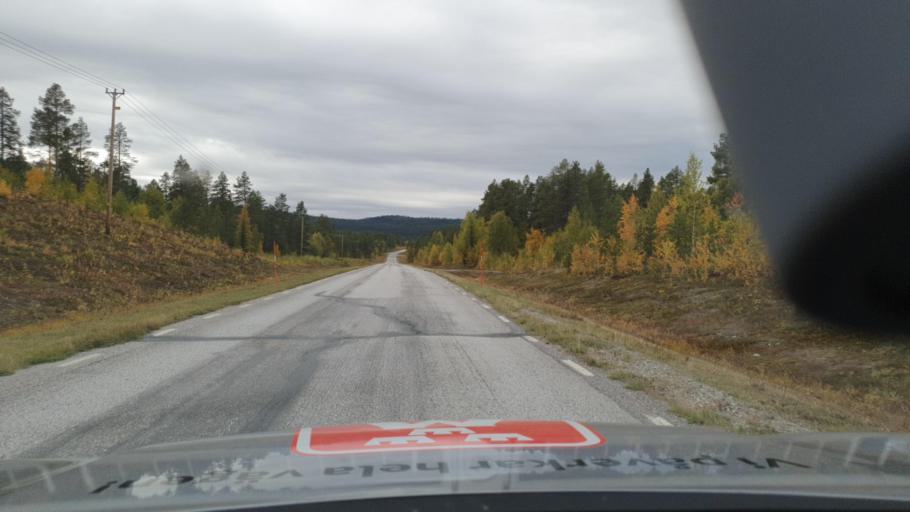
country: SE
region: Norrbotten
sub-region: Arjeplogs Kommun
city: Arjeplog
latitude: 66.1215
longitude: 17.3092
